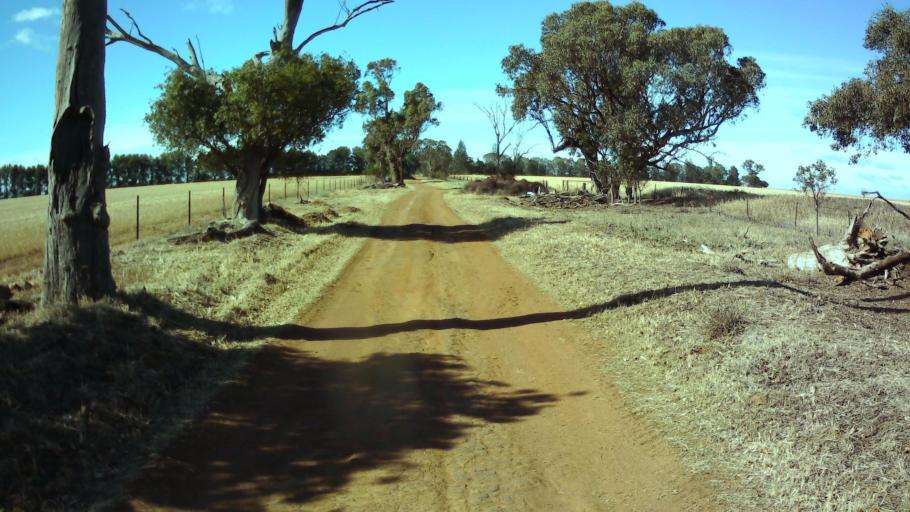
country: AU
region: New South Wales
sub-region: Weddin
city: Grenfell
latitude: -34.0582
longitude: 148.2677
